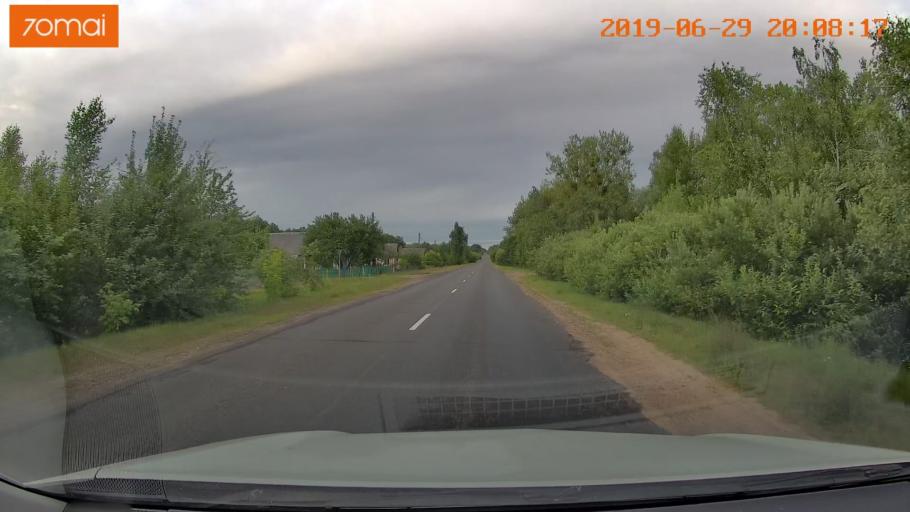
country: BY
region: Brest
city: Lahishyn
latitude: 52.3441
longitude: 26.0547
